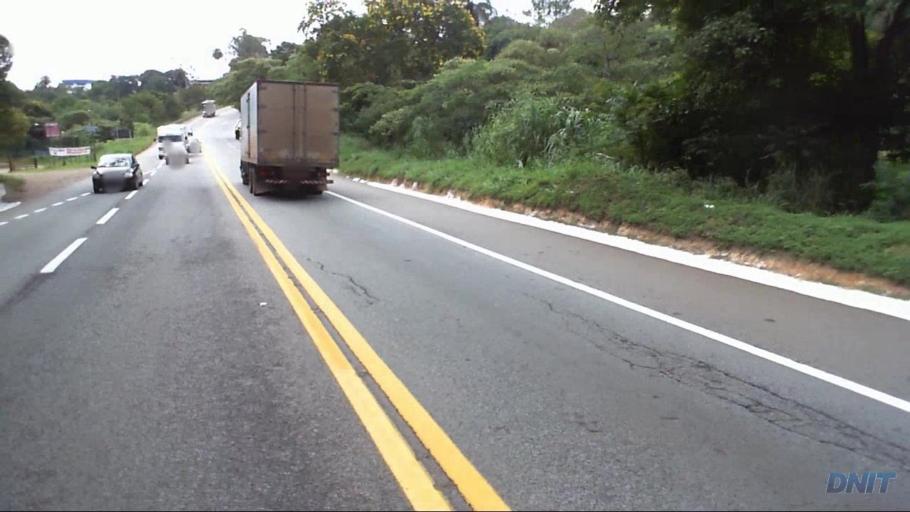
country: BR
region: Minas Gerais
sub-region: Santa Luzia
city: Santa Luzia
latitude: -19.7957
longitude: -43.7477
